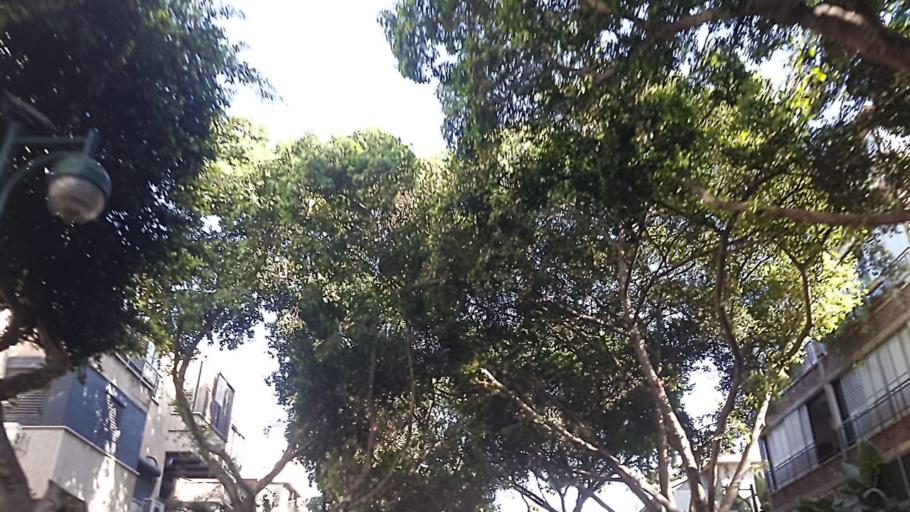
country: IL
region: Tel Aviv
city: Ramat Gan
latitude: 32.0806
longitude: 34.8195
